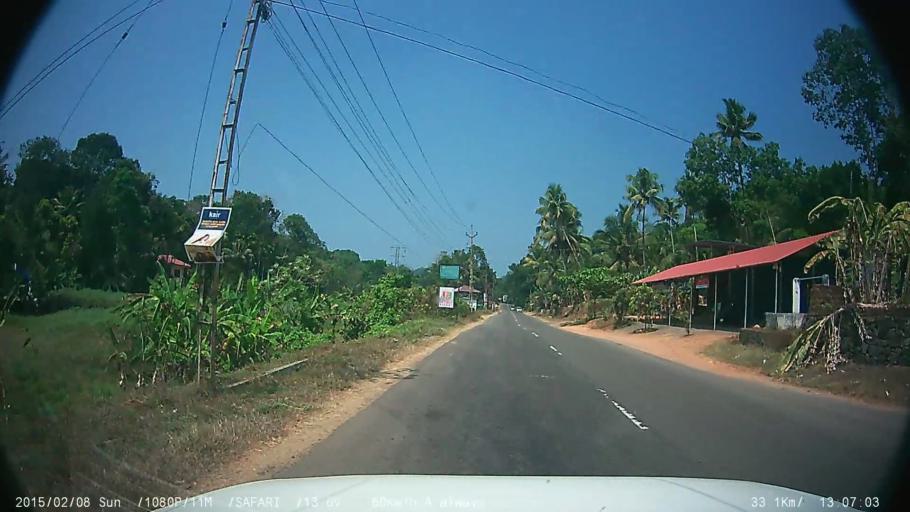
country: IN
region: Kerala
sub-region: Ernakulam
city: Muvattupuzha
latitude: 9.9134
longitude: 76.5833
